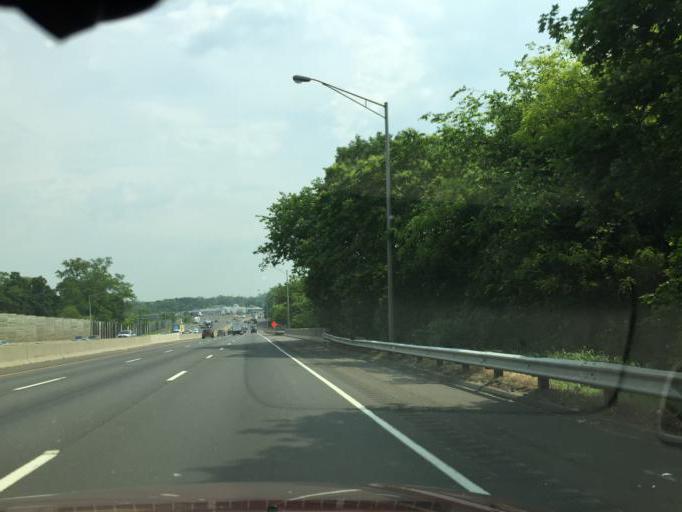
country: US
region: Connecticut
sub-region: Fairfield County
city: Stamford
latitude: 41.0626
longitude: -73.5086
